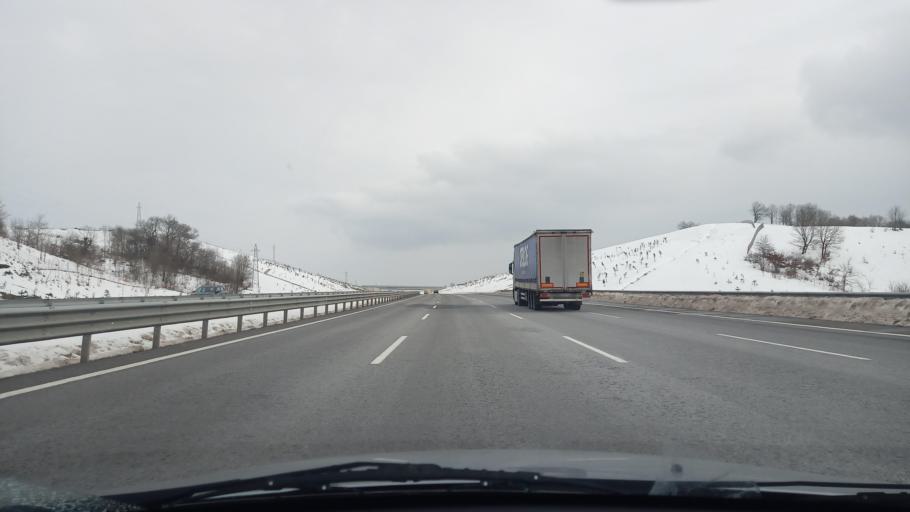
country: TR
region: Kocaeli
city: Korfez
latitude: 40.8639
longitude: 29.8209
